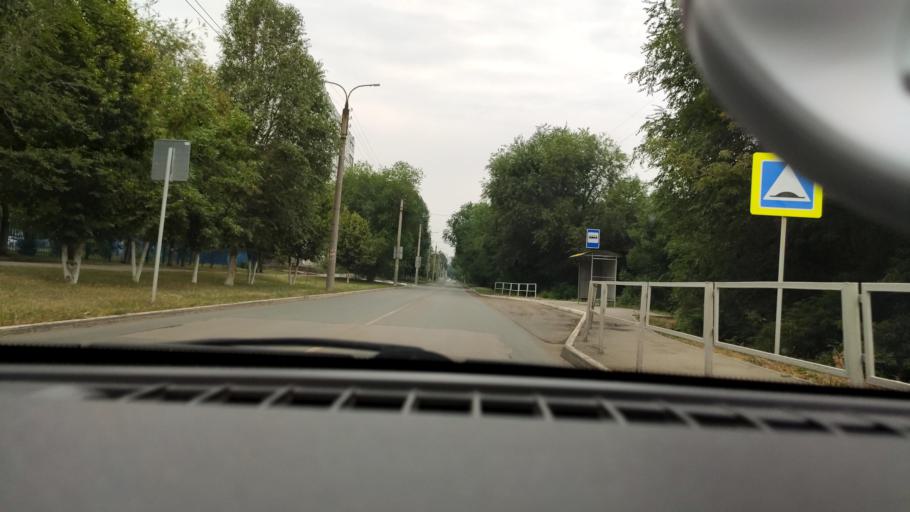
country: RU
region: Samara
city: Novokuybyshevsk
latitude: 53.0935
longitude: 49.9903
